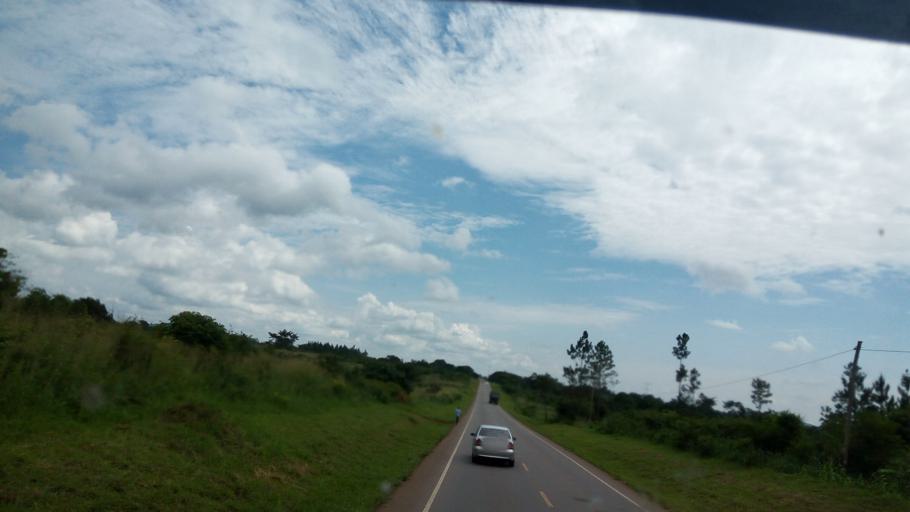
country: UG
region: Central Region
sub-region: Nakasongola District
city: Nakasongola
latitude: 1.2276
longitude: 32.4647
